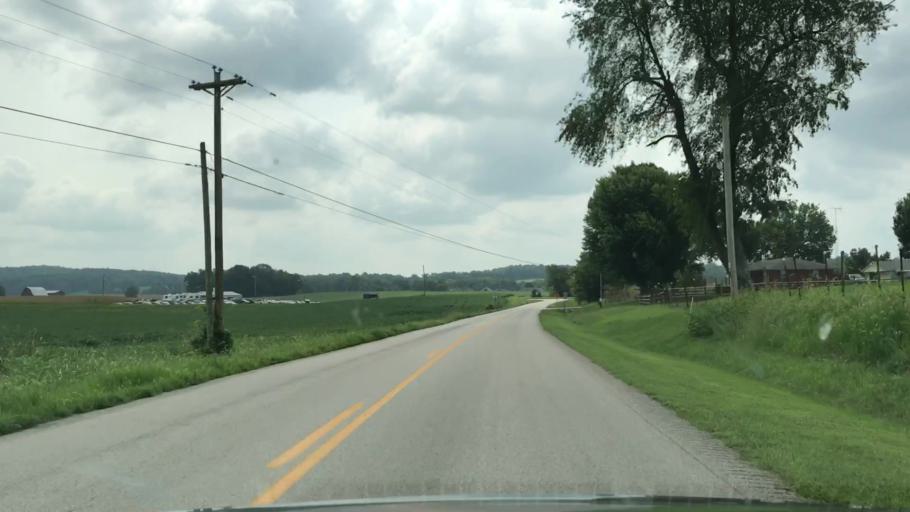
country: US
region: Kentucky
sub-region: Barren County
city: Cave City
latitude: 37.0990
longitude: -85.9754
